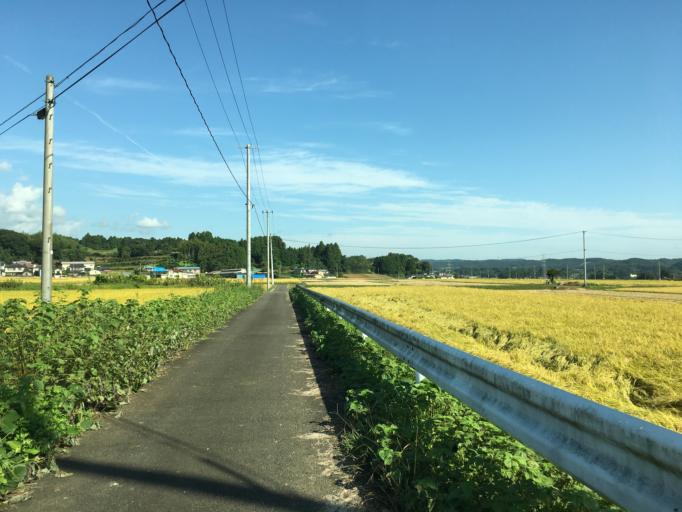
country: JP
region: Fukushima
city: Motomiya
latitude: 37.5495
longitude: 140.3817
